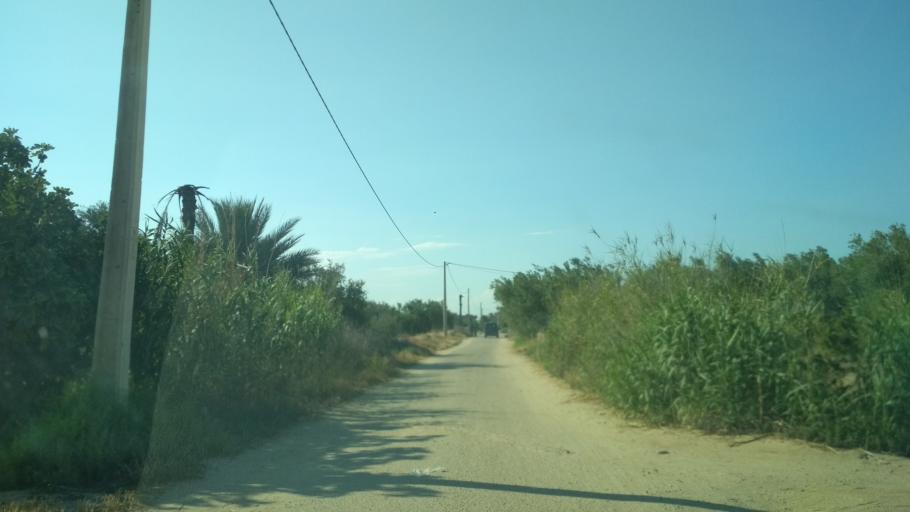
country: TN
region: Qabis
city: Gabes
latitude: 33.9524
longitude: 10.0603
